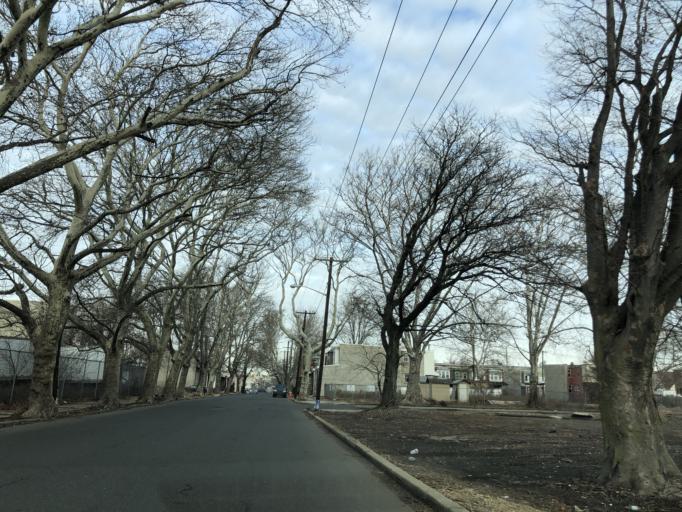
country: US
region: New Jersey
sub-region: Camden County
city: Camden
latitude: 39.9267
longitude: -75.1215
